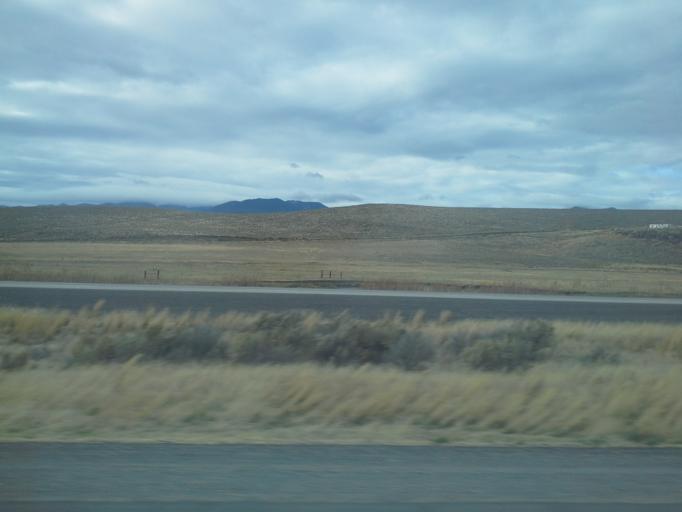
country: US
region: Oregon
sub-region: Baker County
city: Baker City
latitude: 44.9772
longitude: -117.8851
